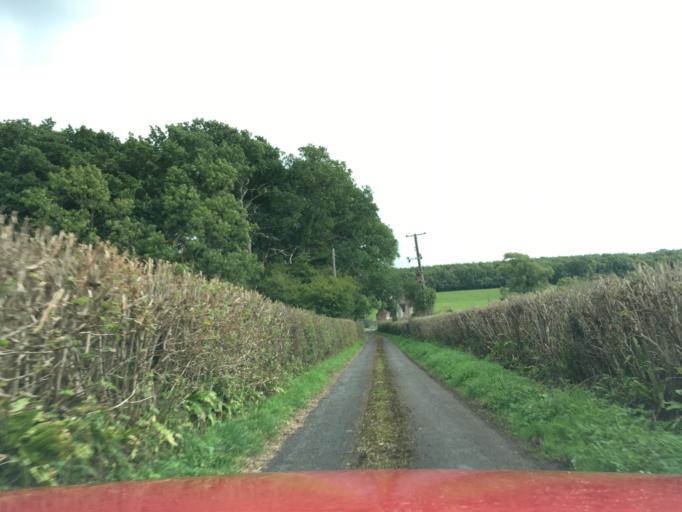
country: GB
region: England
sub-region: South Gloucestershire
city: Falfield
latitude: 51.6271
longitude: -2.4551
